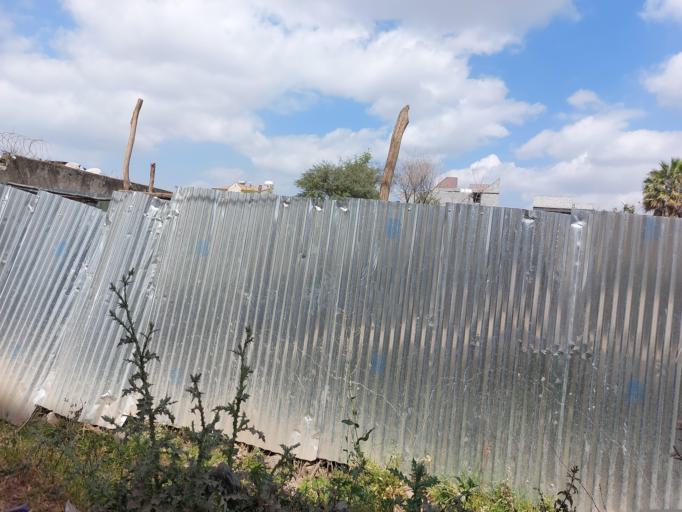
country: ET
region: Adis Abeba
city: Addis Ababa
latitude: 8.9598
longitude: 38.7312
